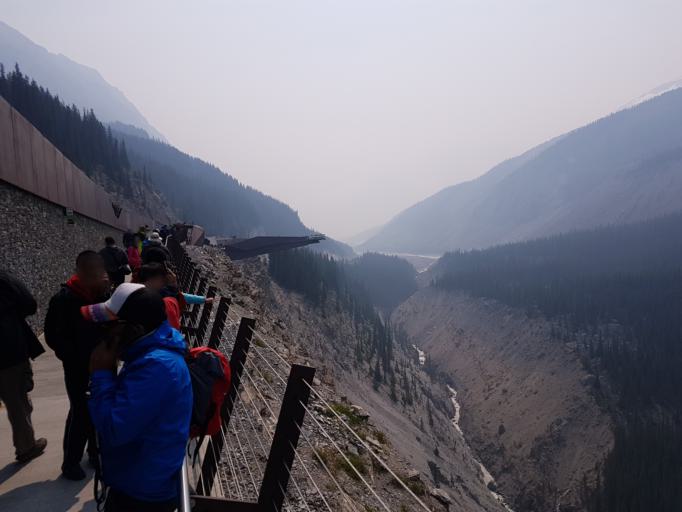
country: CA
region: Alberta
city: Jasper Park Lodge
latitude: 52.2602
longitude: -117.2789
